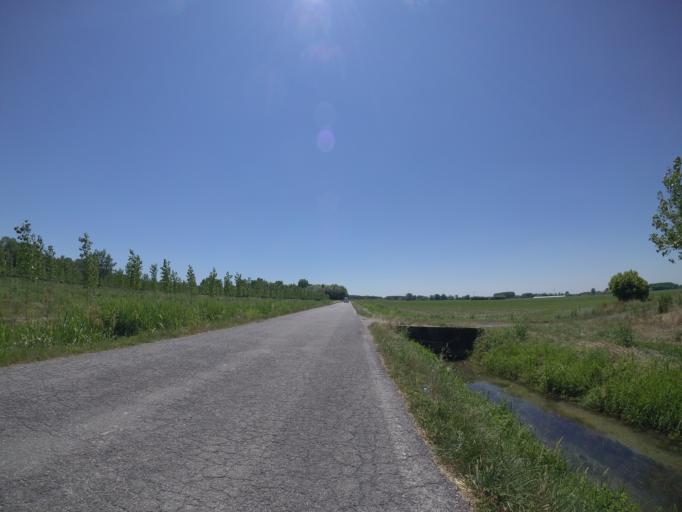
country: IT
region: Friuli Venezia Giulia
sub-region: Provincia di Udine
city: Teor
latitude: 45.8682
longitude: 13.0788
